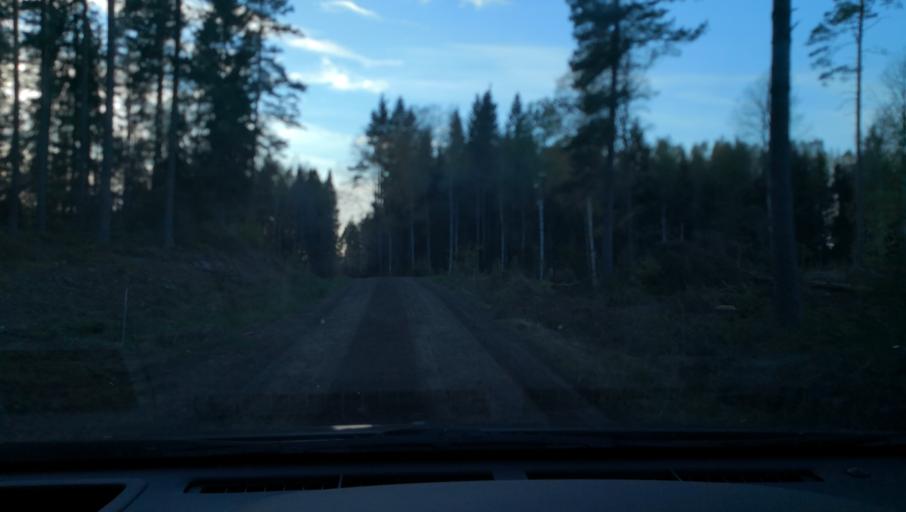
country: SE
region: OErebro
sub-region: Askersunds Kommun
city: Asbro
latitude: 58.8851
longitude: 15.1267
